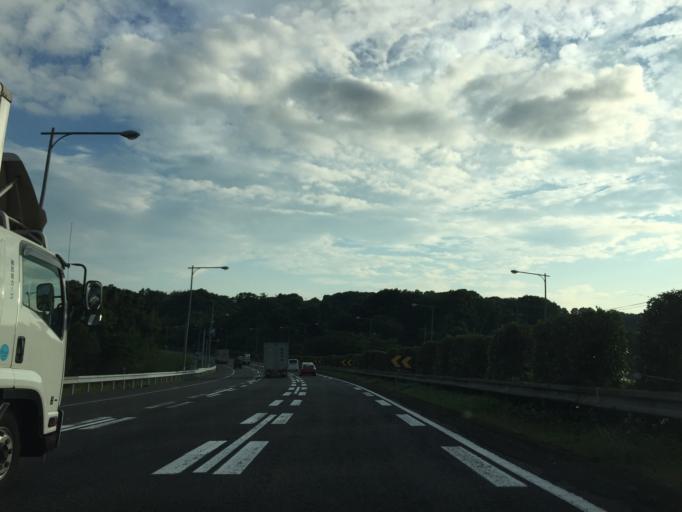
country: JP
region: Kanagawa
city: Hadano
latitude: 35.3501
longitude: 139.2067
